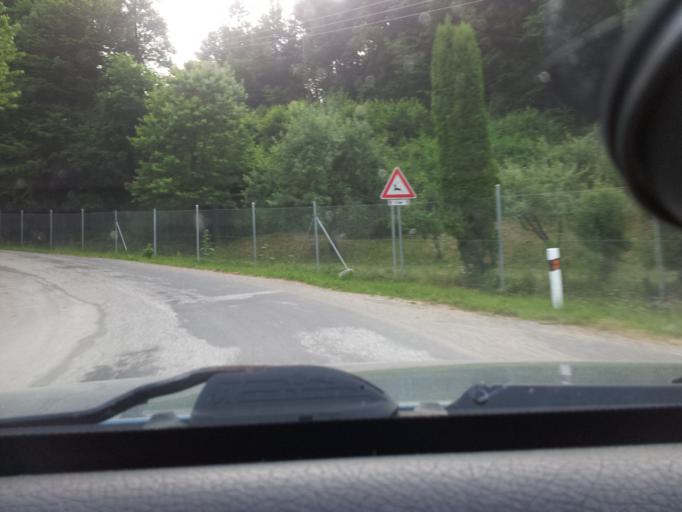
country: SK
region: Banskobystricky
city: Zarnovica
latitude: 48.3879
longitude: 18.7756
